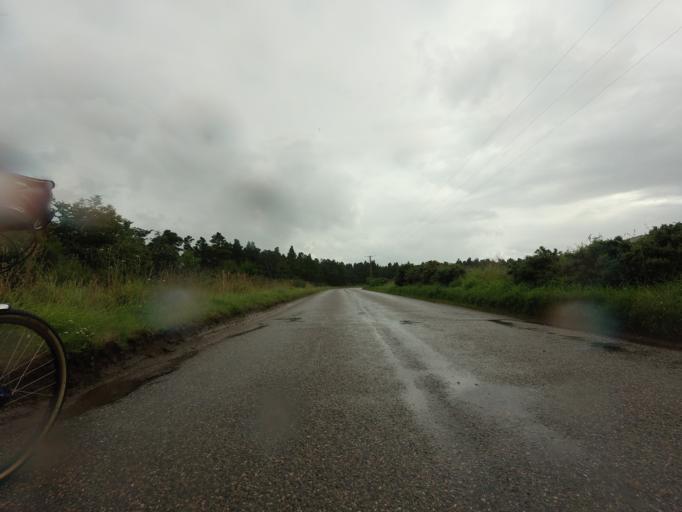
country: GB
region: Scotland
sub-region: Moray
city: Fochabers
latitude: 57.6575
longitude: -3.0574
